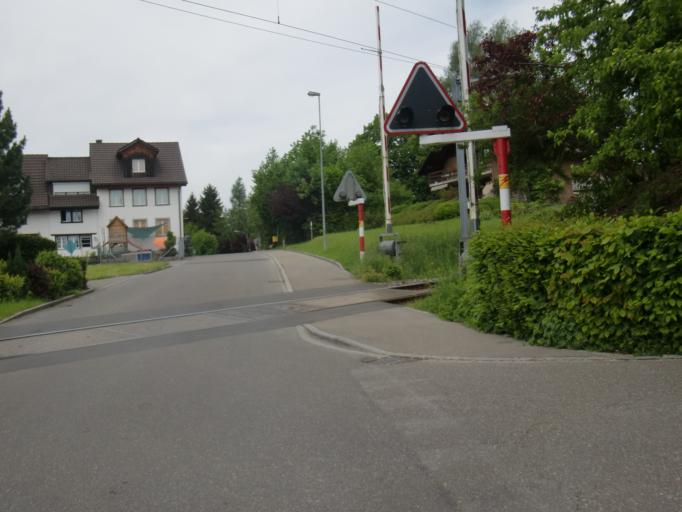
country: CH
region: Zurich
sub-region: Bezirk Hinwil
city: Tann / Tann (Dorfkern)
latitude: 47.2659
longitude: 8.8458
